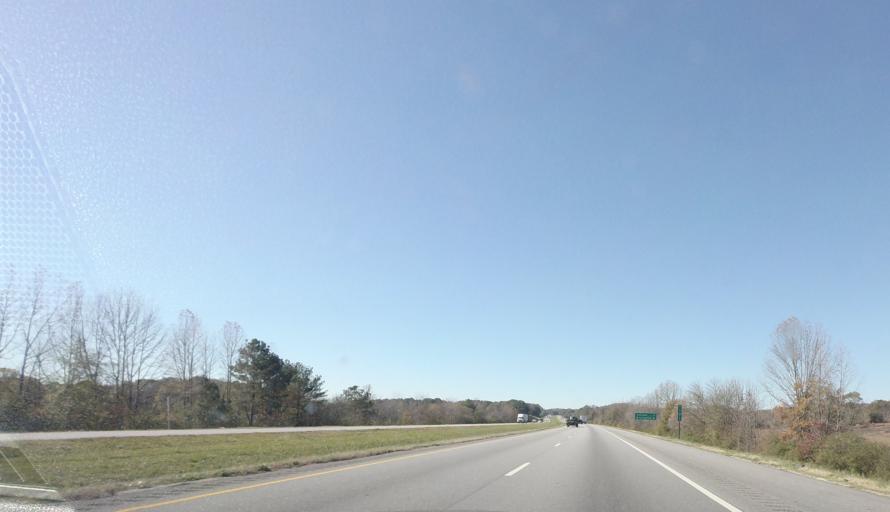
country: US
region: Alabama
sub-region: Calhoun County
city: Choccolocco
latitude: 33.6164
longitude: -85.7374
